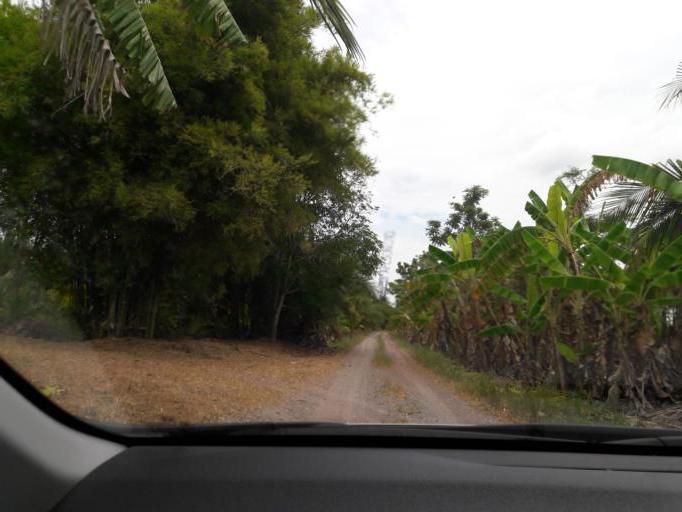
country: TH
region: Ratchaburi
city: Damnoen Saduak
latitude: 13.5565
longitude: 100.0012
